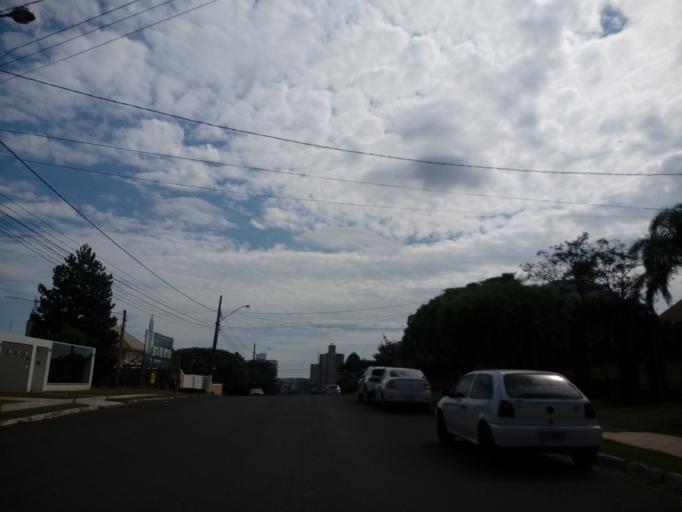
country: BR
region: Santa Catarina
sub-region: Chapeco
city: Chapeco
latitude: -27.1054
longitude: -52.6045
